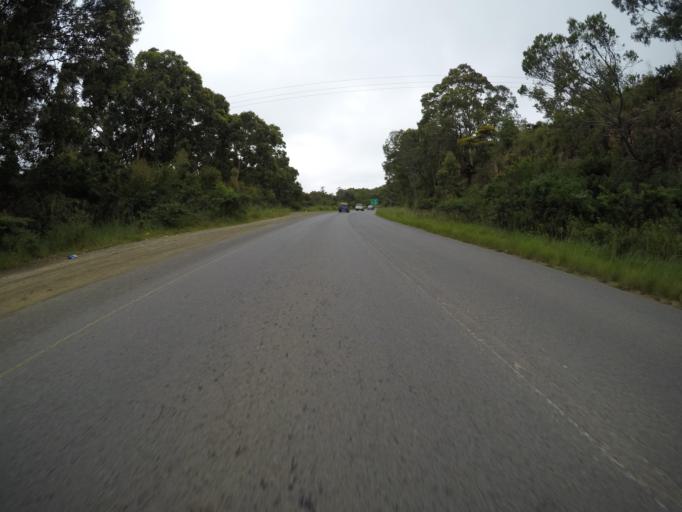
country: ZA
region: Eastern Cape
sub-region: Buffalo City Metropolitan Municipality
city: East London
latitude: -32.9364
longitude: 27.9455
